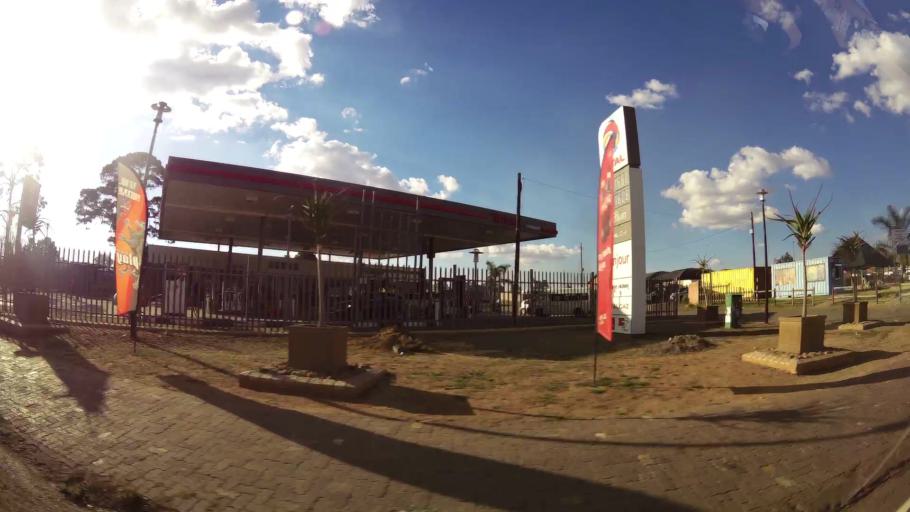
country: ZA
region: Mpumalanga
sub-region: Nkangala District Municipality
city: Witbank
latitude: -25.8688
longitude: 29.1696
